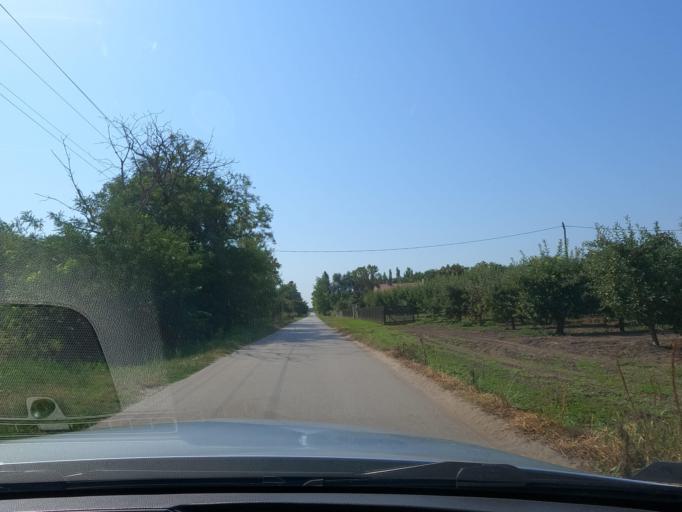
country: HU
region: Csongrad
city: Asotthalom
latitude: 46.0946
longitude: 19.7805
